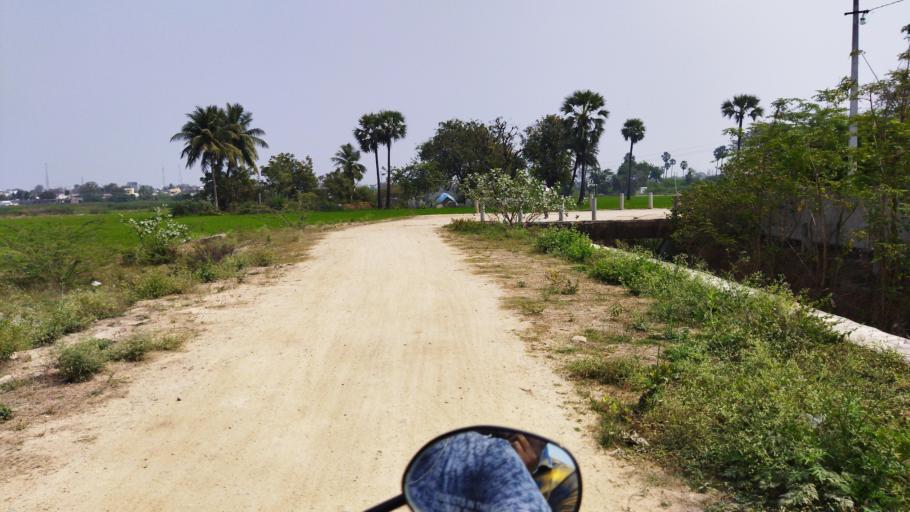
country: IN
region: Telangana
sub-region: Nalgonda
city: Nalgonda
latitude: 17.1609
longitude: 79.4182
